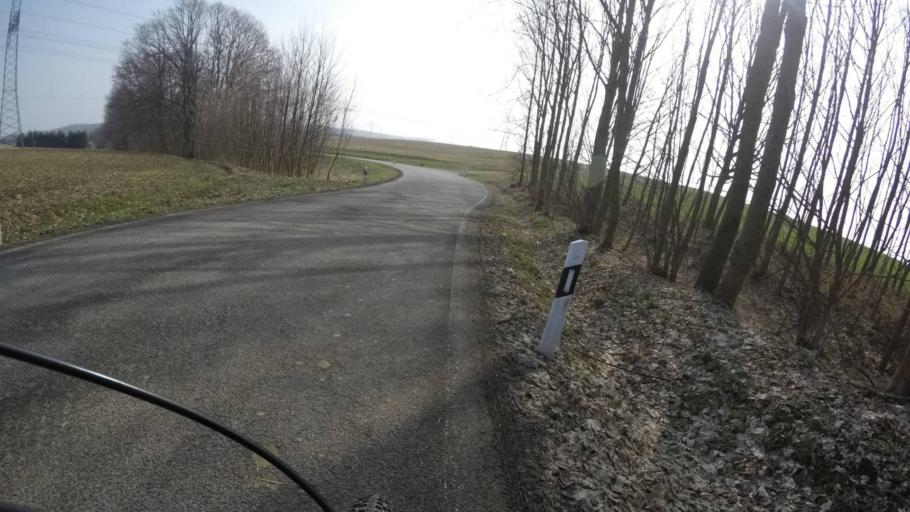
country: DE
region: Saxony
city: Callenberg
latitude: 50.8797
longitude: 12.6448
